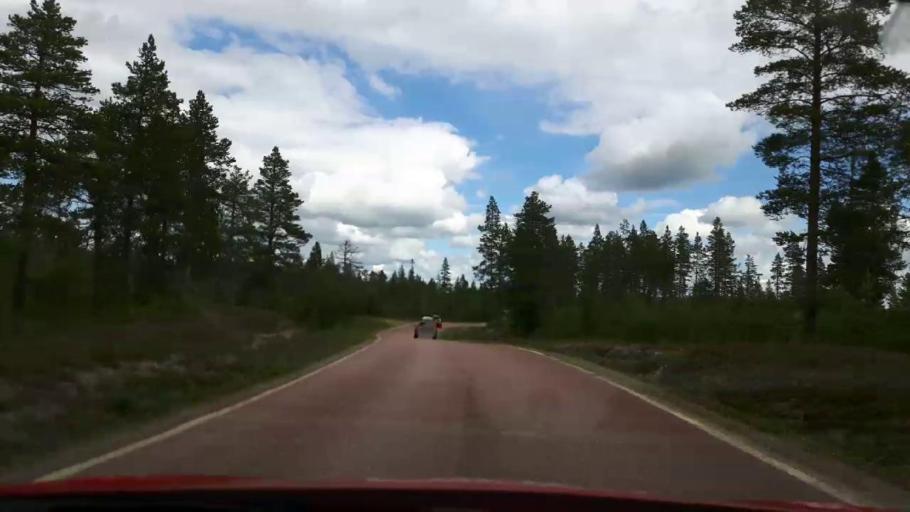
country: NO
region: Hedmark
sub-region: Trysil
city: Innbygda
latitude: 61.8754
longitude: 12.9644
